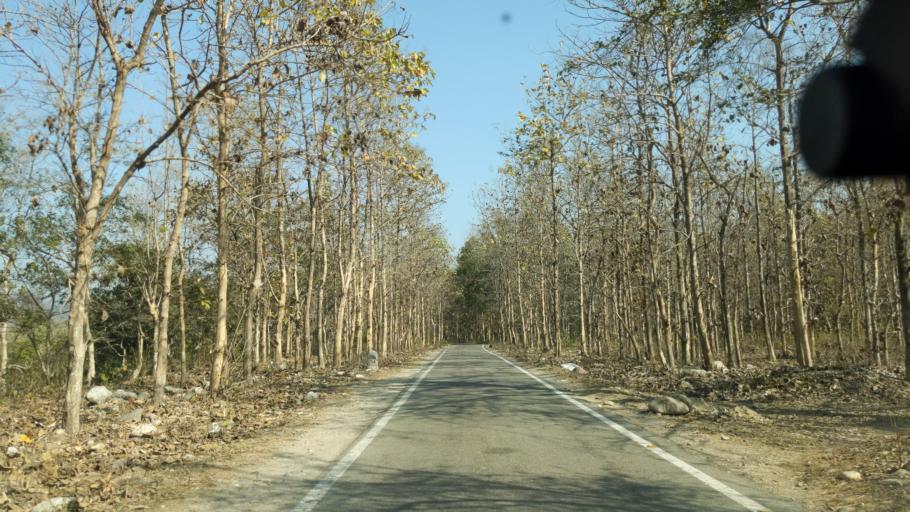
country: IN
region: Uttarakhand
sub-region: Naini Tal
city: Ramnagar
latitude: 29.4237
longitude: 79.1389
